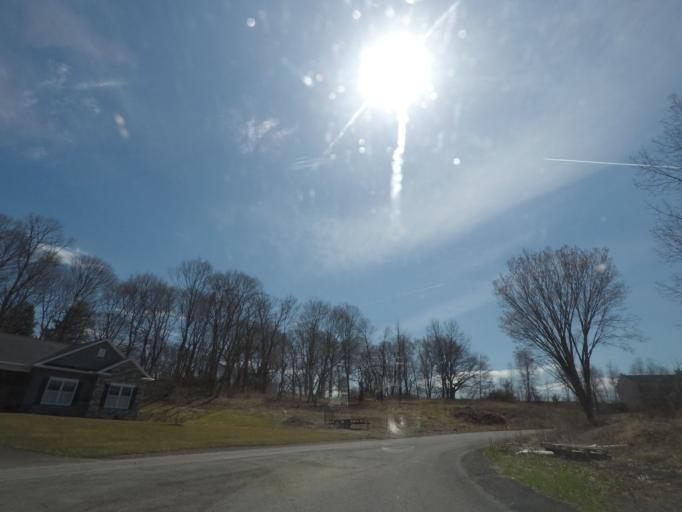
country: US
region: New York
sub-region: Rensselaer County
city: Wynantskill
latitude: 42.6953
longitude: -73.6602
